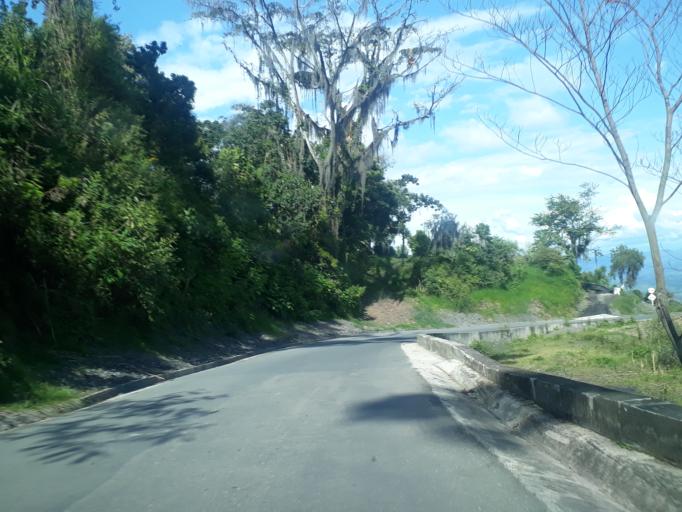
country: CO
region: Santander
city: Velez
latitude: 6.0336
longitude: -73.6548
